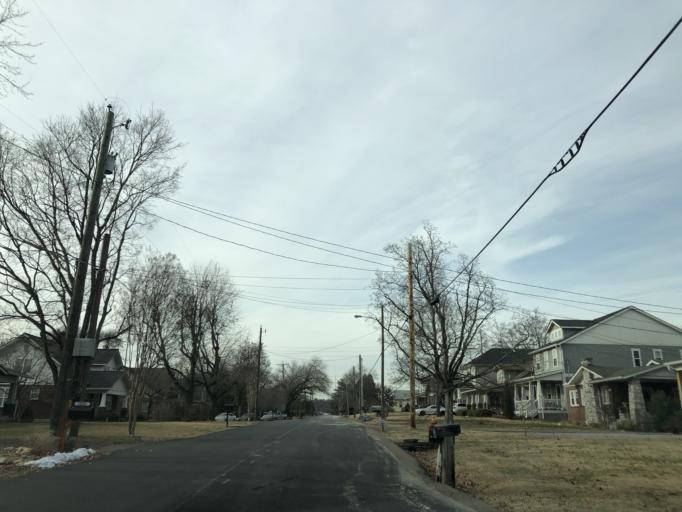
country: US
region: Tennessee
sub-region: Davidson County
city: Nashville
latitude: 36.2123
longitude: -86.7234
